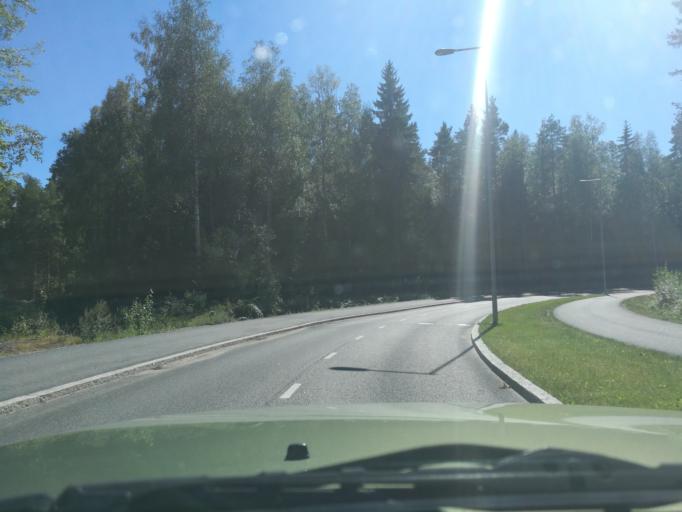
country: FI
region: Uusimaa
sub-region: Helsinki
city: Kerava
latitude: 60.3528
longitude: 25.1372
